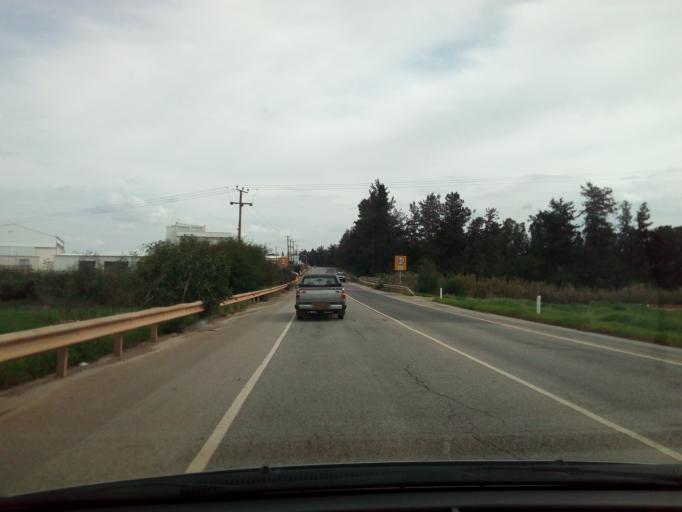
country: CY
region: Lefkosia
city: Akaki
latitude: 35.1356
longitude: 33.1130
